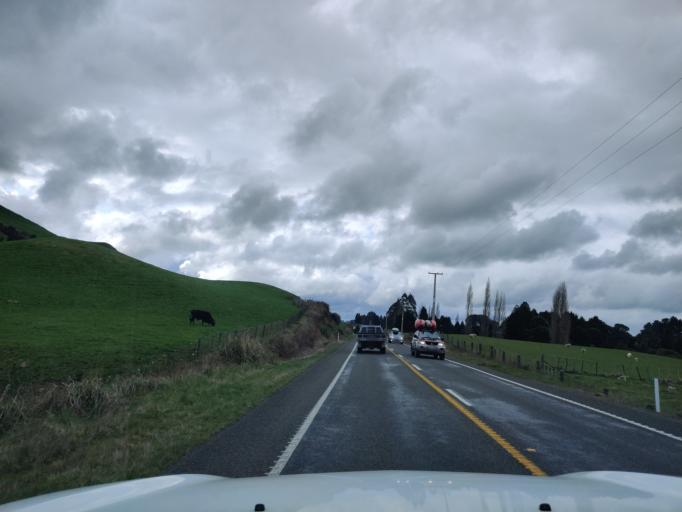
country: NZ
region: Manawatu-Wanganui
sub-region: Ruapehu District
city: Waiouru
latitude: -39.4599
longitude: 175.2939
